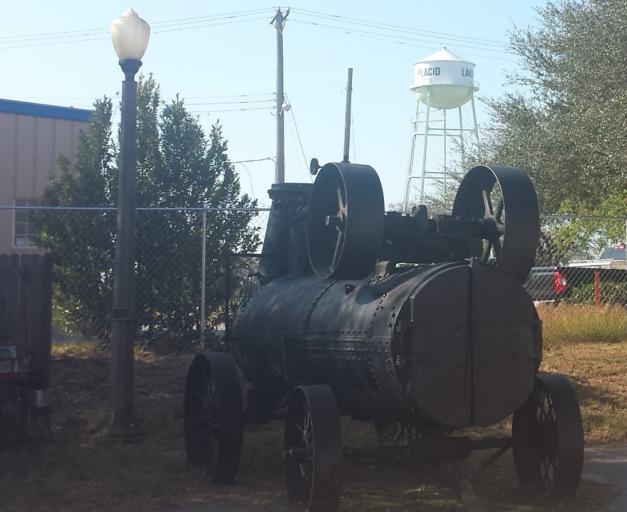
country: US
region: Florida
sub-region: Highlands County
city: Lake Placid
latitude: 27.2980
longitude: -81.3670
